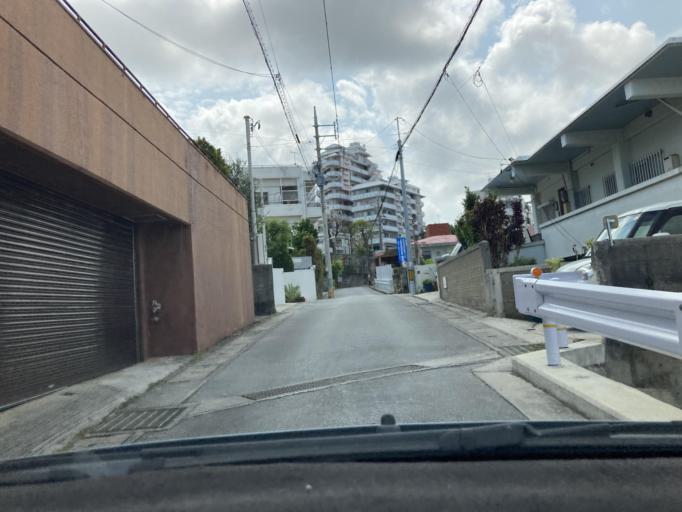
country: JP
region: Okinawa
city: Naha-shi
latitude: 26.2231
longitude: 127.7128
